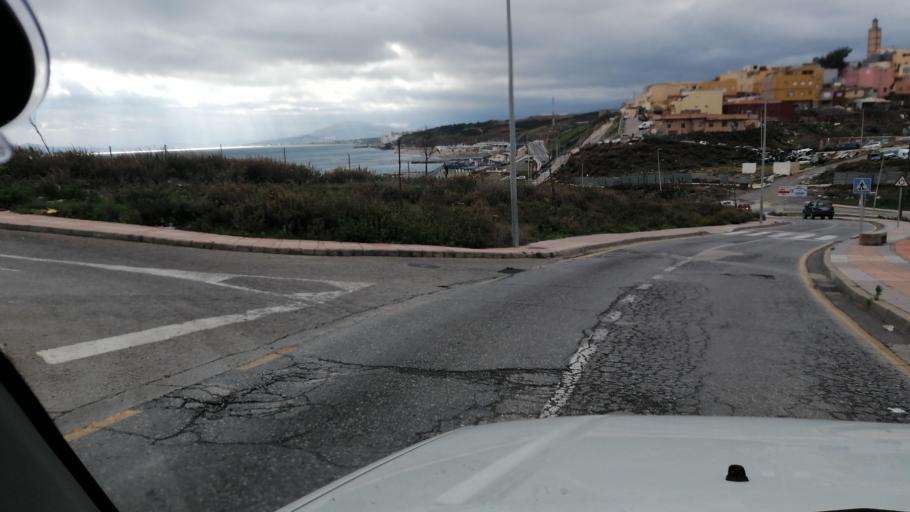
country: ES
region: Ceuta
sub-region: Ceuta
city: Ceuta
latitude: 35.8782
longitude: -5.3405
